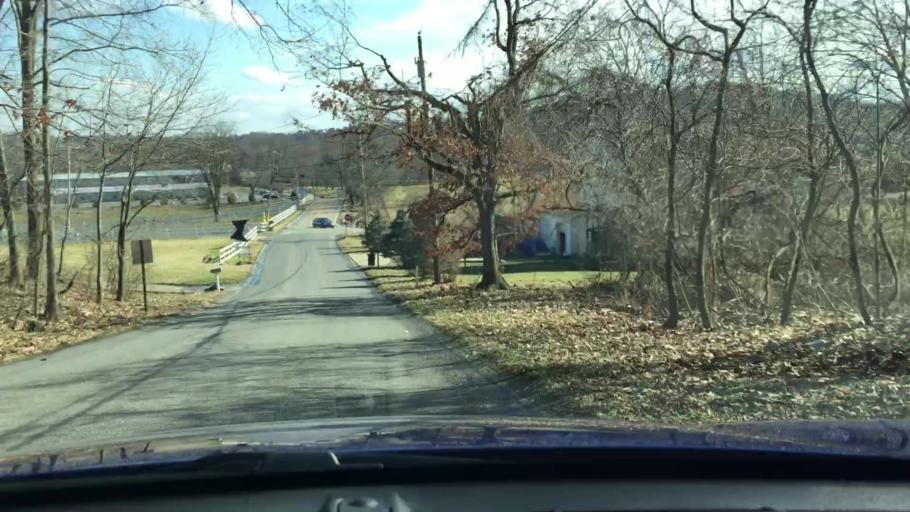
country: US
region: Pennsylvania
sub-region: Washington County
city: Thompsonville
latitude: 40.3080
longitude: -80.1378
